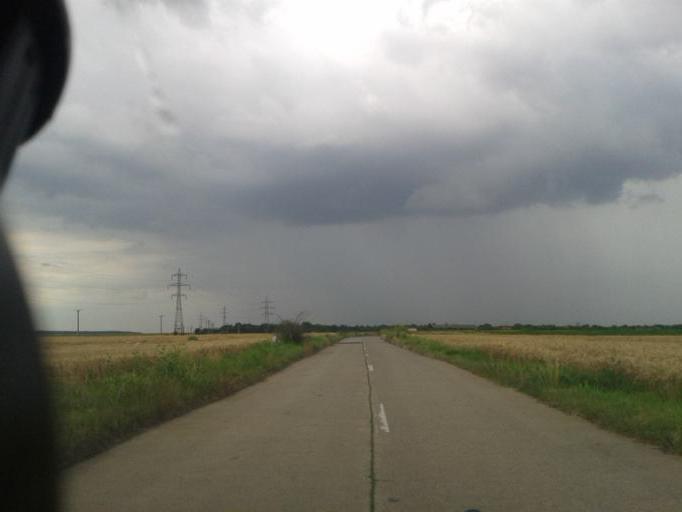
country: RO
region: Calarasi
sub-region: Comuna Belciugatele
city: Belciugatele
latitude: 44.5428
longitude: 26.4496
